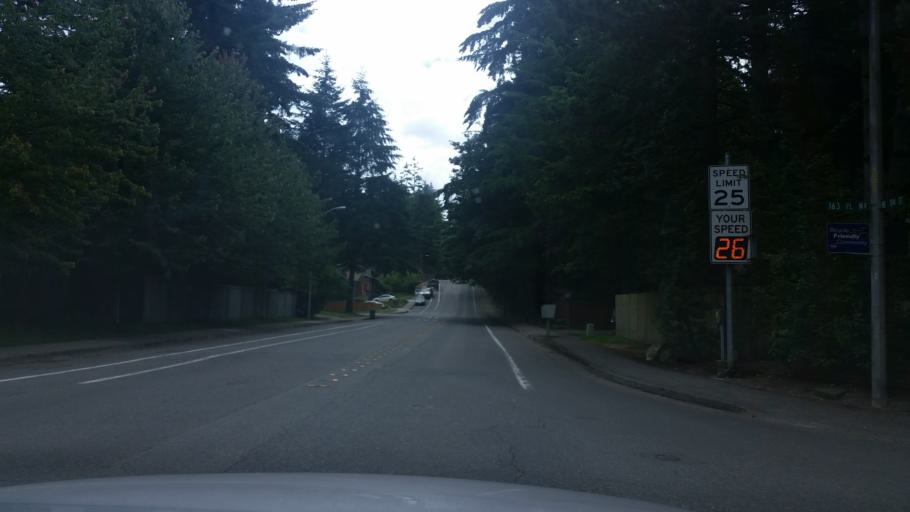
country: US
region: Washington
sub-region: King County
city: Redmond
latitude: 47.6929
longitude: -122.1224
